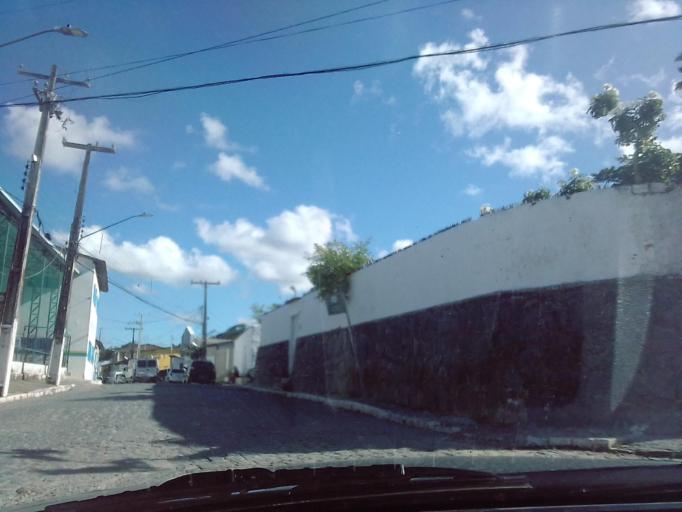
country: BR
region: Pernambuco
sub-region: Igarassu
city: Igarassu
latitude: -7.8498
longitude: -34.8431
